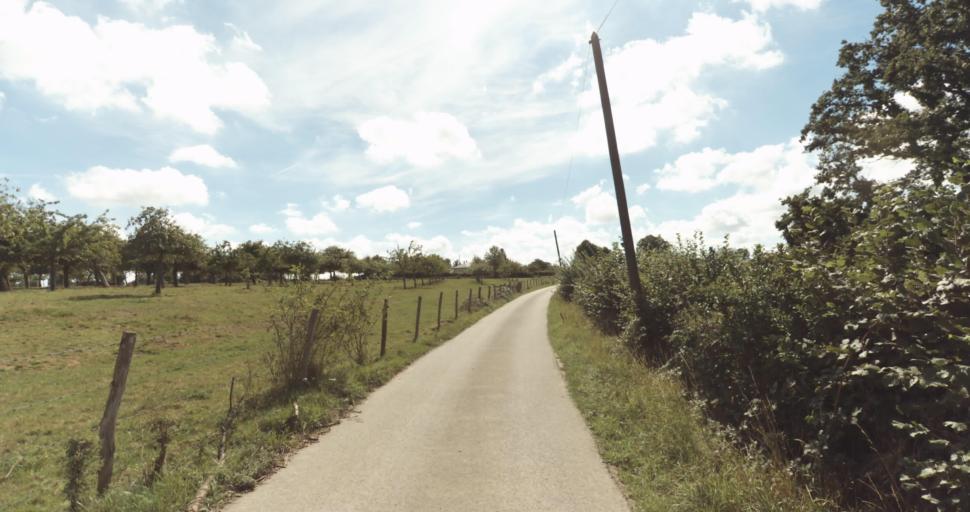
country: FR
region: Lower Normandy
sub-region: Departement du Calvados
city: Orbec
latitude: 48.9465
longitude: 0.3894
